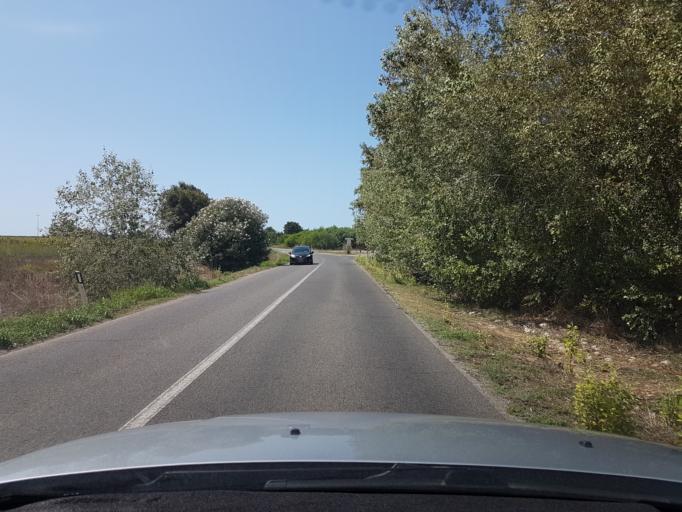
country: IT
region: Sardinia
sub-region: Provincia di Oristano
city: Riola Sardo
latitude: 40.0219
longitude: 8.4795
